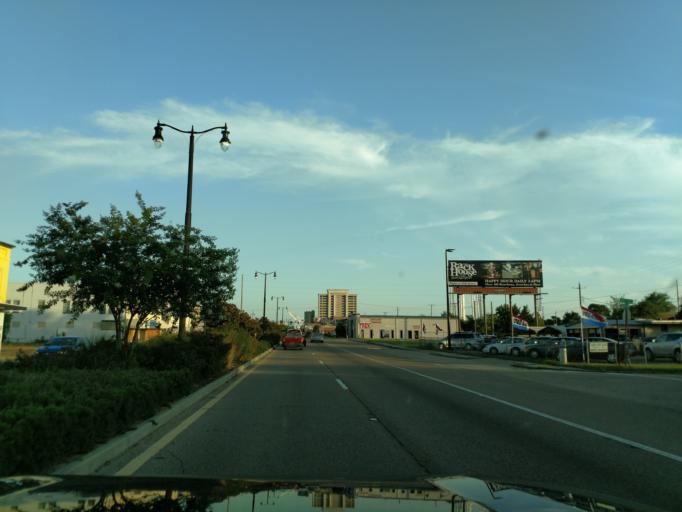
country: US
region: Mississippi
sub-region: Harrison County
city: Gulfport
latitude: 30.3756
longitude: -89.0931
